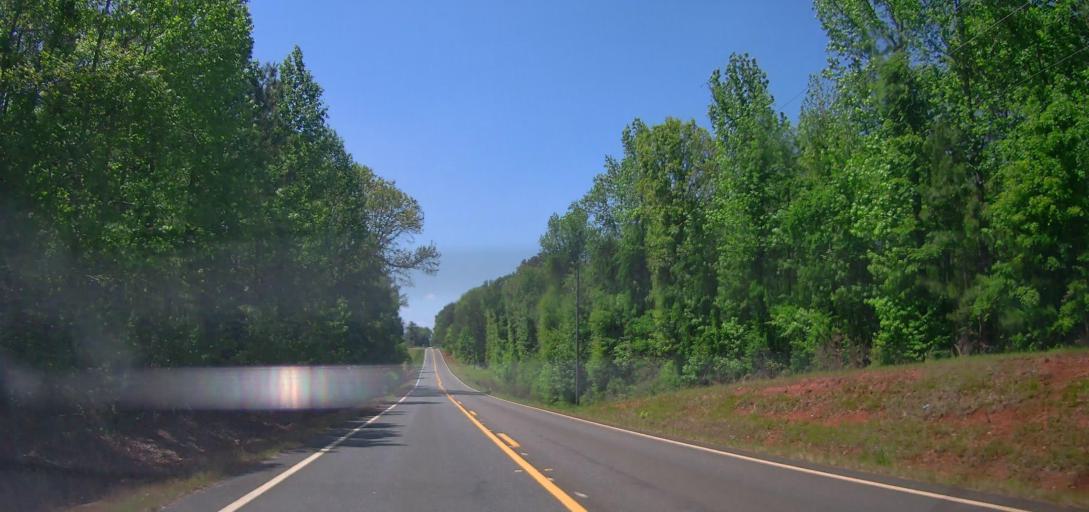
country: US
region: Georgia
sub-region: Jasper County
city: Monticello
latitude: 33.2916
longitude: -83.6389
